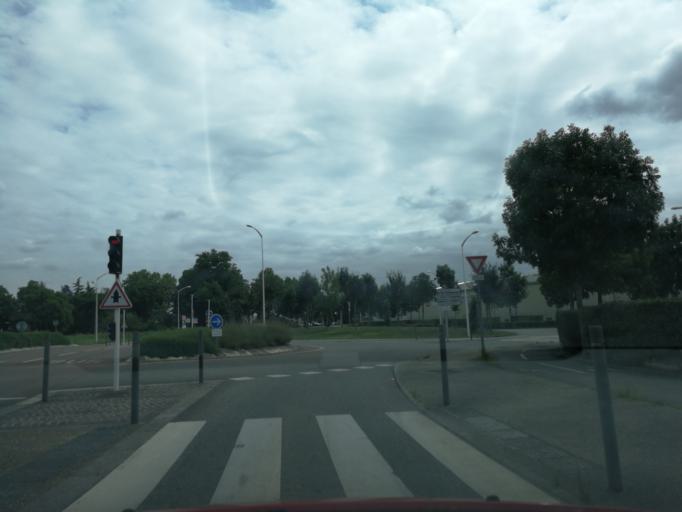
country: FR
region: Midi-Pyrenees
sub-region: Departement de la Haute-Garonne
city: Balma
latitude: 43.5967
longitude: 1.4968
